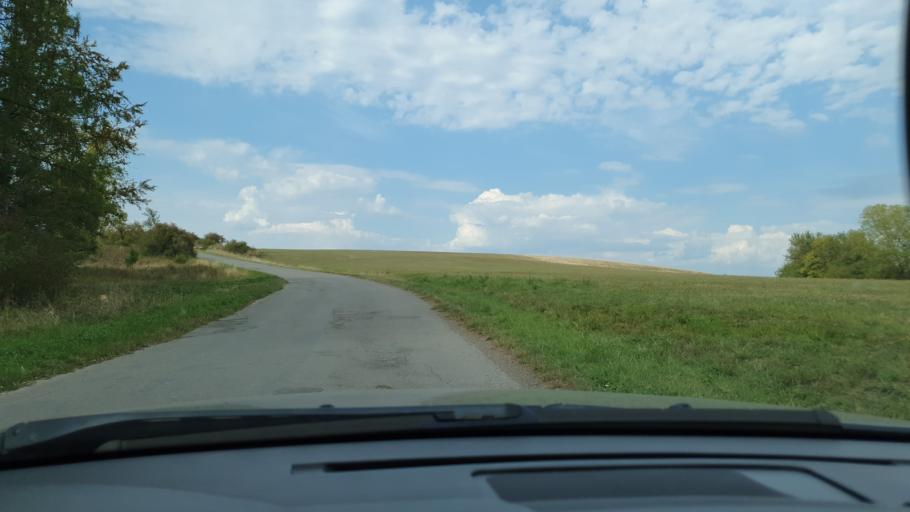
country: DE
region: Rheinland-Pfalz
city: Grossbundenbach
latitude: 49.2708
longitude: 7.3987
